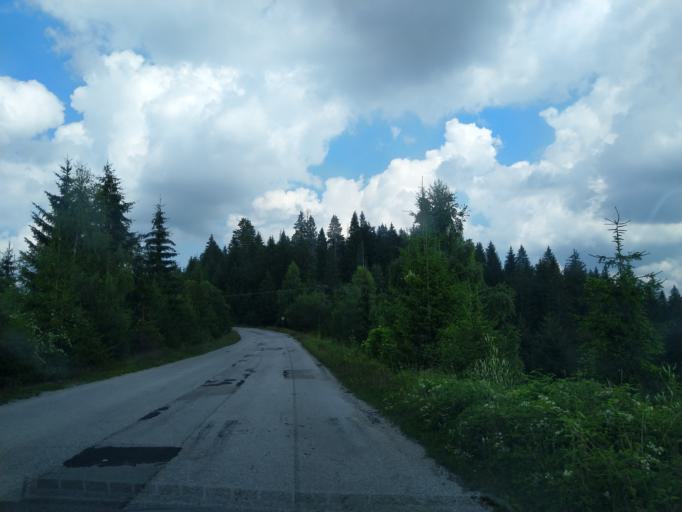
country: RS
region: Central Serbia
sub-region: Zlatiborski Okrug
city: Nova Varos
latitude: 43.5264
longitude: 19.8774
